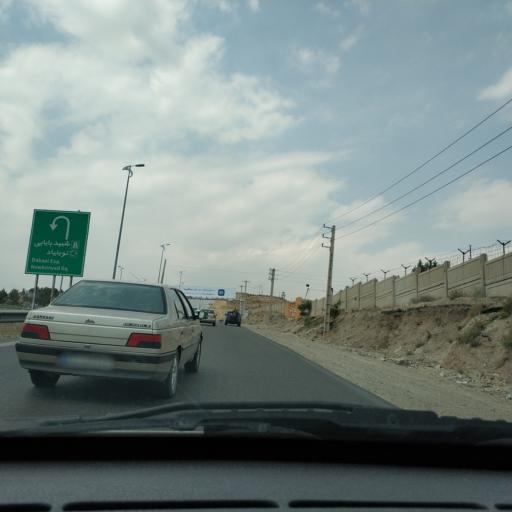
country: IR
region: Tehran
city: Tajrish
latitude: 35.7835
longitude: 51.5649
